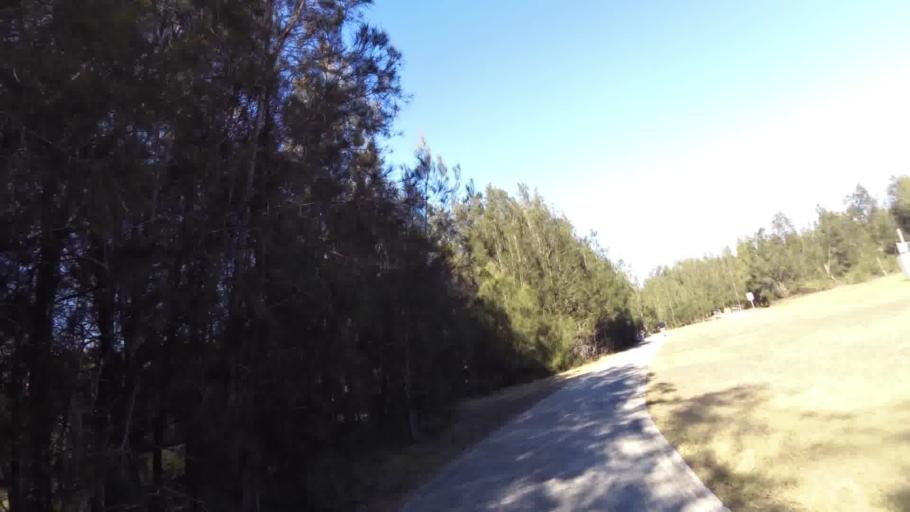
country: AU
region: New South Wales
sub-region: Wollongong
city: Berkeley
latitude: -34.4851
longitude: 150.8391
